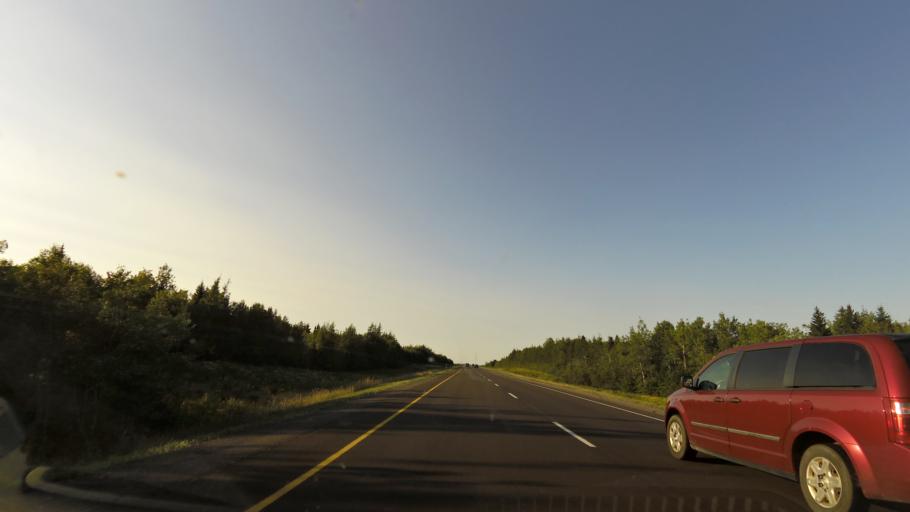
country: CA
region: New Brunswick
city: Dieppe
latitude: 46.0581
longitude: -64.5870
